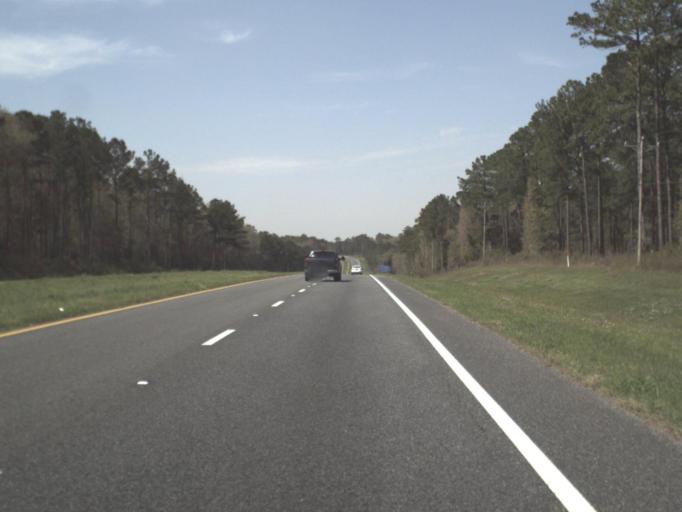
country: US
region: Florida
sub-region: Gadsden County
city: Midway
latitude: 30.5416
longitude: -84.4804
